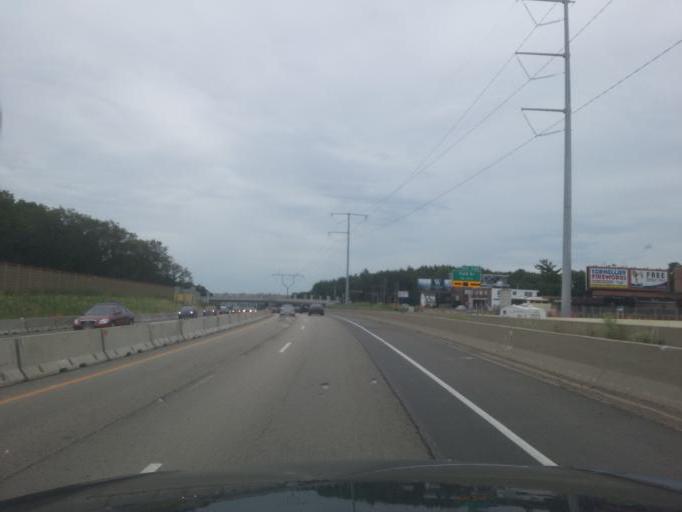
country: US
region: Wisconsin
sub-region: Dane County
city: Shorewood Hills
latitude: 43.0348
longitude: -89.4469
